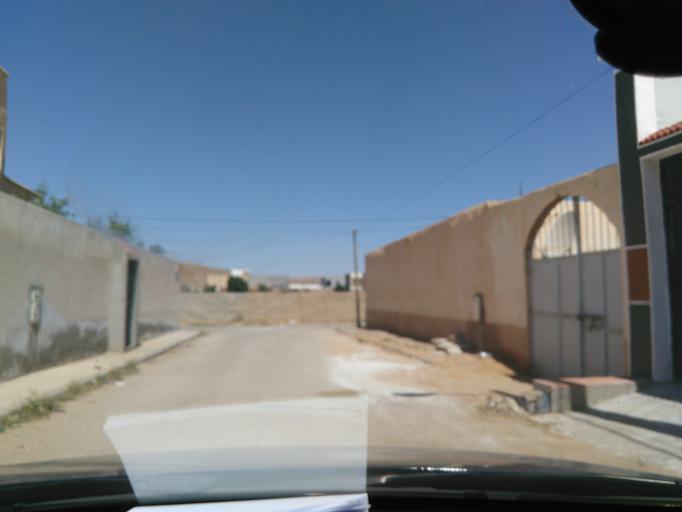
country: TN
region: Tataouine
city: Tataouine
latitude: 32.9499
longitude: 10.4670
